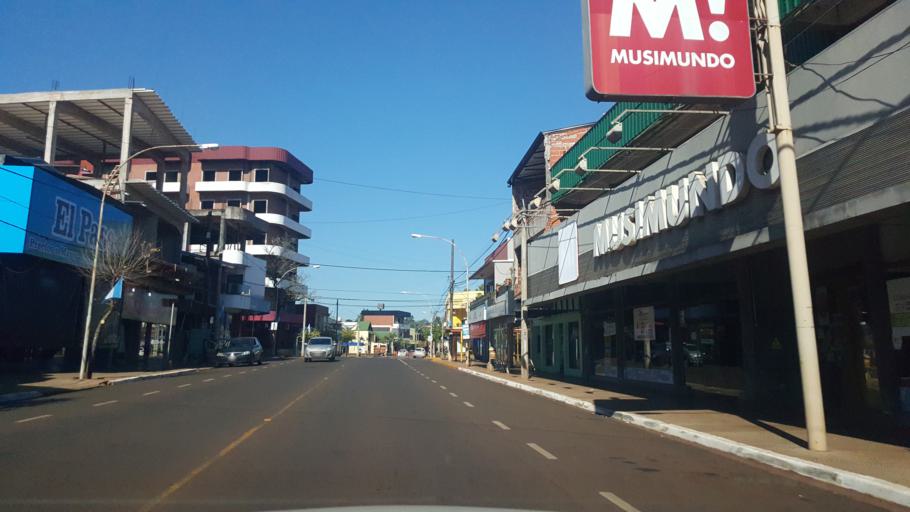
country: AR
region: Misiones
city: Puerto Rico
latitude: -26.8112
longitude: -55.0256
